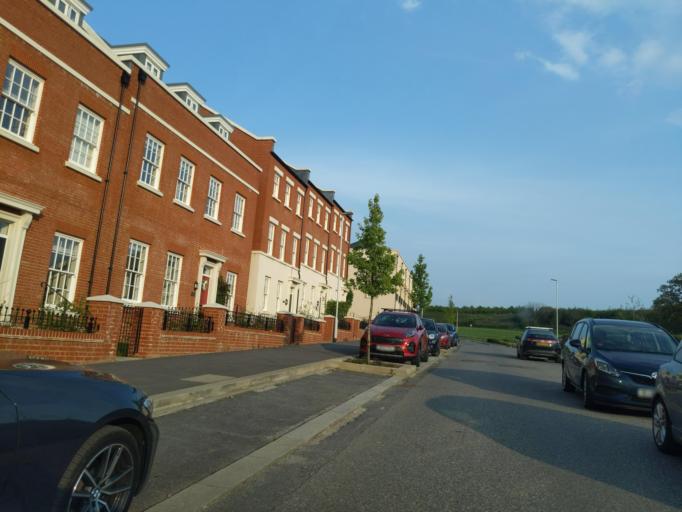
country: GB
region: England
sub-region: Devon
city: Plympton
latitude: 50.3631
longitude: -4.0512
